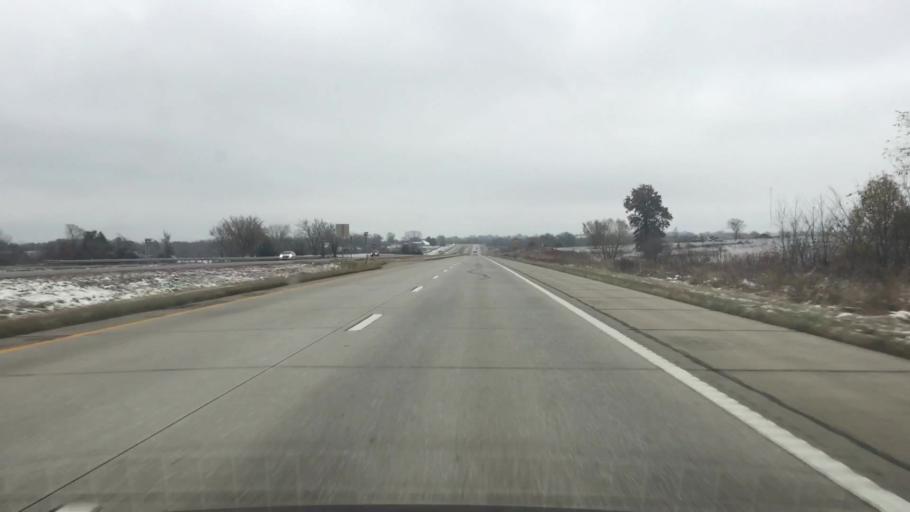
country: US
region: Missouri
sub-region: Saint Clair County
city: Osceola
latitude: 38.2014
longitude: -93.7494
